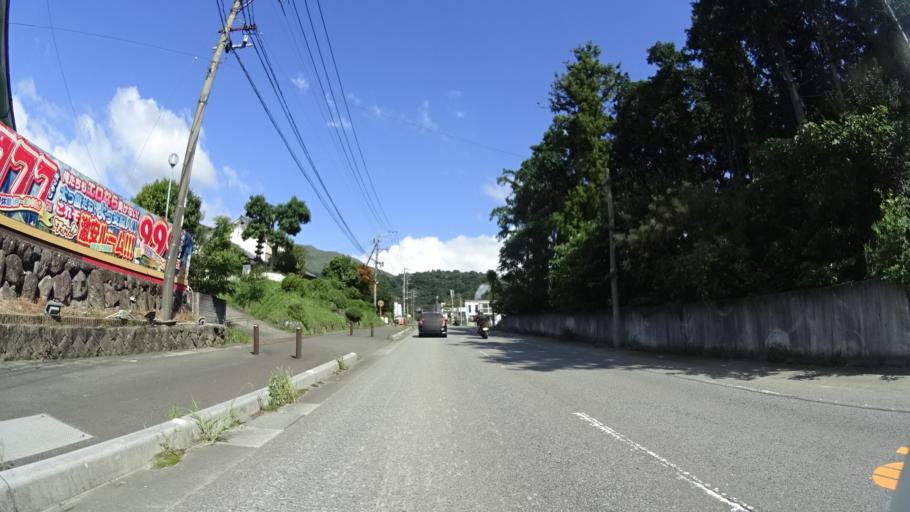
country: JP
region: Oita
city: Beppu
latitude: 33.3115
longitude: 131.4609
